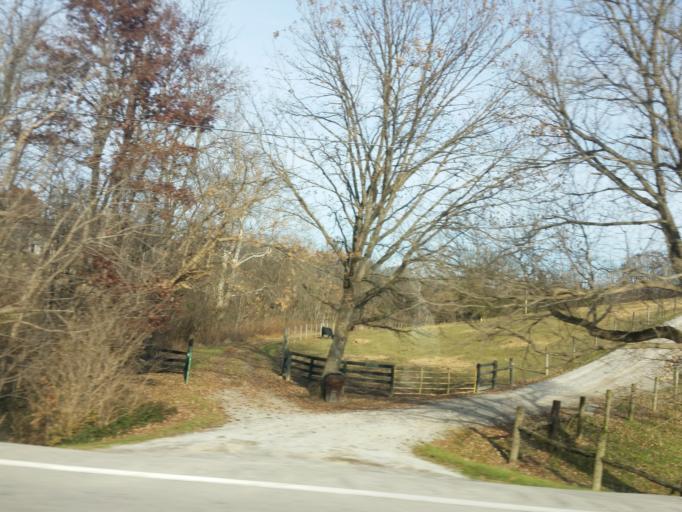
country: US
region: Kentucky
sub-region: Harrison County
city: Cynthiana
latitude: 38.4981
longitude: -84.2879
